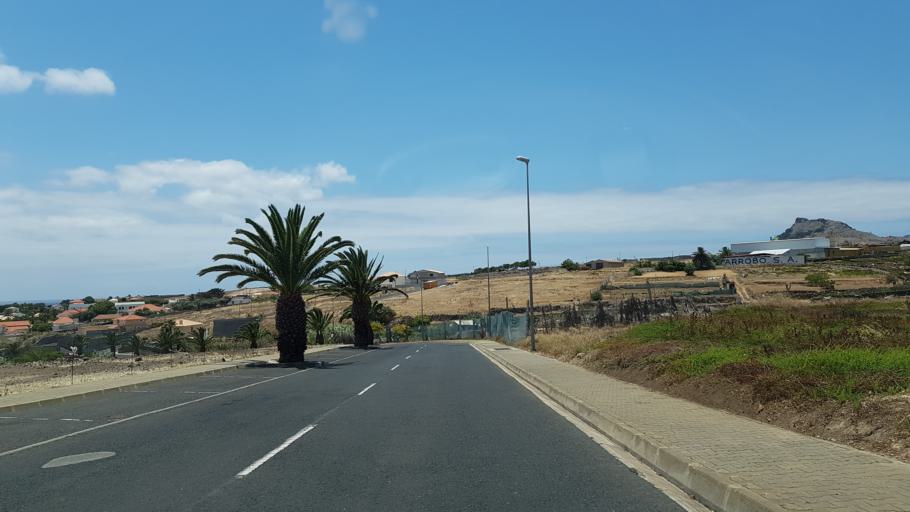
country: PT
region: Madeira
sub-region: Porto Santo
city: Vila de Porto Santo
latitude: 33.0635
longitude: -16.3437
